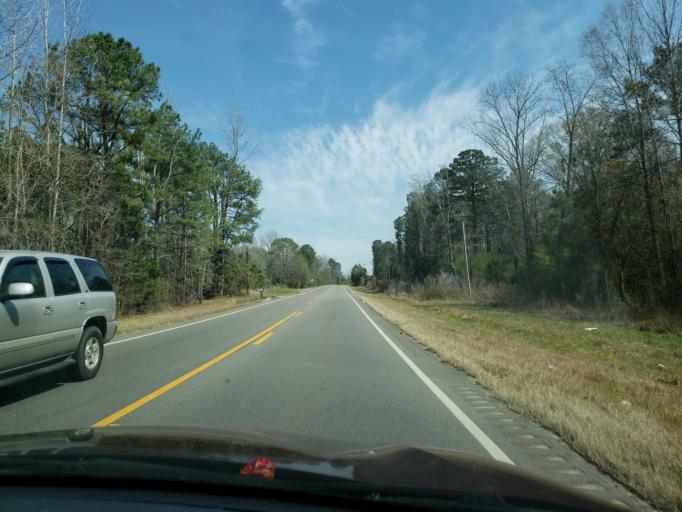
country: US
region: Alabama
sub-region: Elmore County
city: Wetumpka
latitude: 32.5639
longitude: -86.1364
